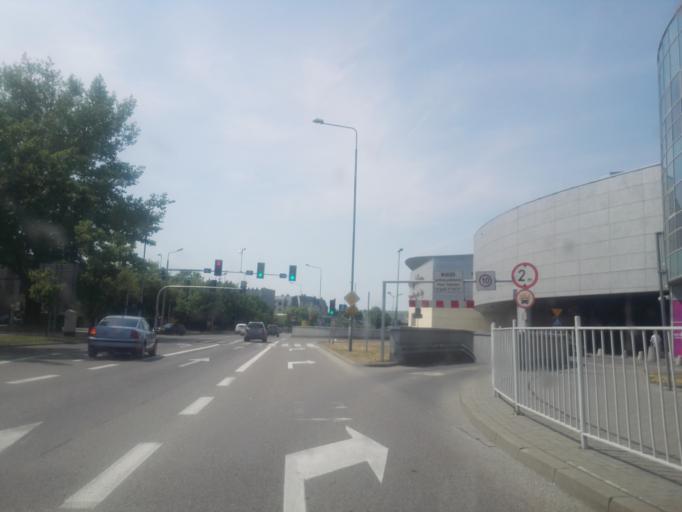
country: PL
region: Podlasie
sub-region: Suwalki
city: Suwalki
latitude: 54.1074
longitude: 22.9352
